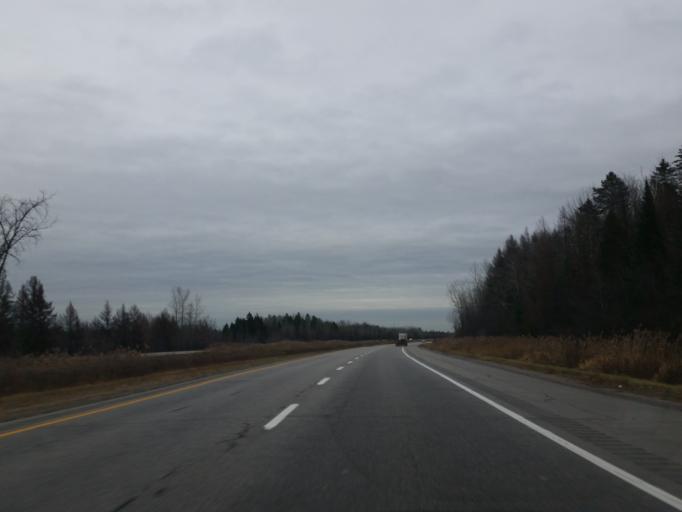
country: CA
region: Quebec
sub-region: Capitale-Nationale
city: Saint-Marc-des-Carrieres
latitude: 46.5983
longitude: -72.1490
